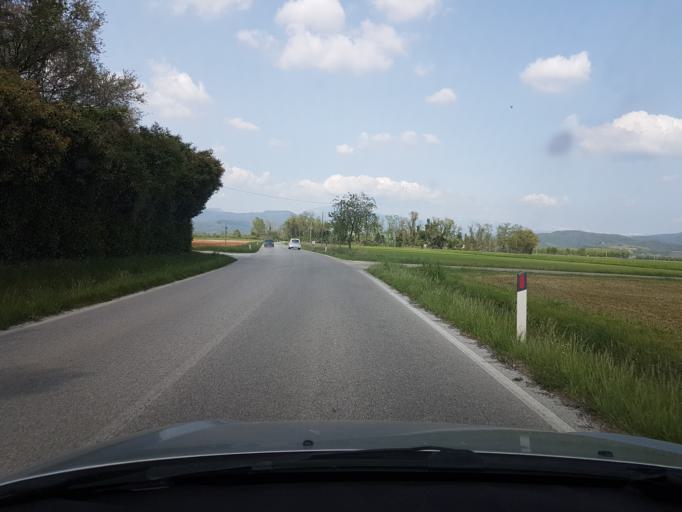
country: IT
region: Friuli Venezia Giulia
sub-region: Provincia di Udine
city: Premariacco
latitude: 46.0575
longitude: 13.4147
